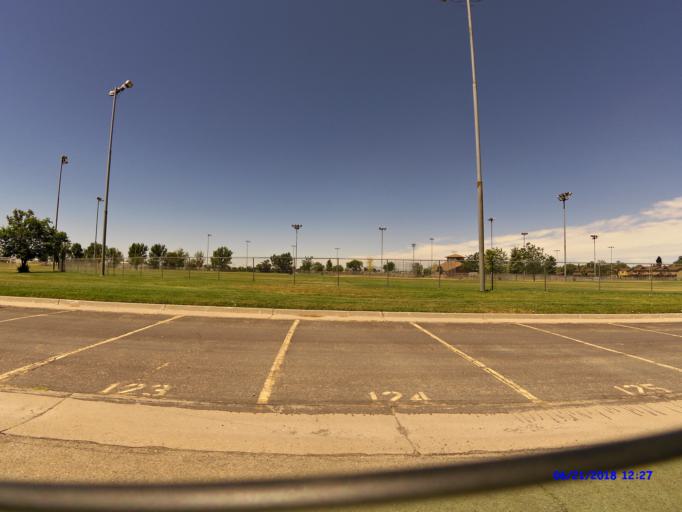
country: US
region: Utah
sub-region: Weber County
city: Harrisville
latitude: 41.2805
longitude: -111.9972
